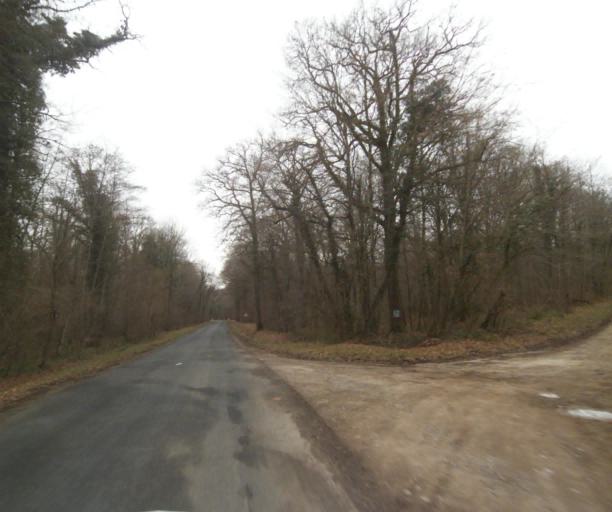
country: FR
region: Champagne-Ardenne
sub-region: Departement de la Haute-Marne
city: Bienville
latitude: 48.5643
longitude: 5.0090
